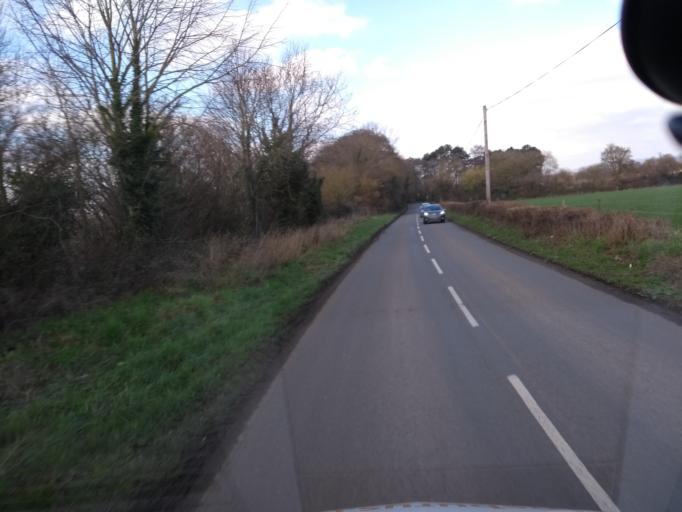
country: GB
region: England
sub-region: Somerset
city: Taunton
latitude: 50.9888
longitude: -3.0718
